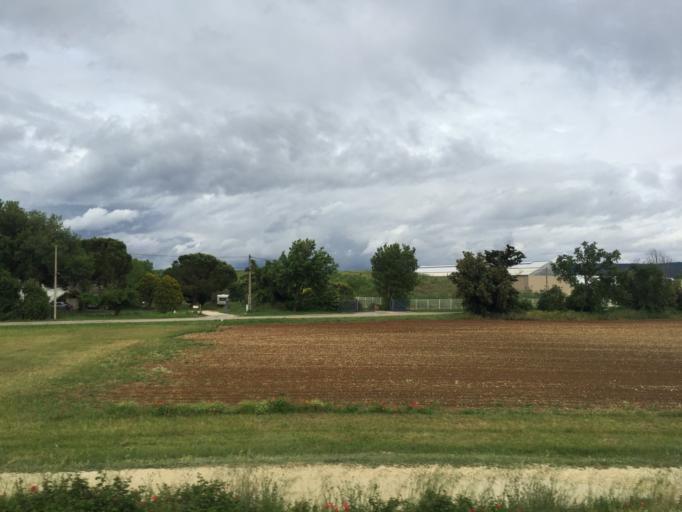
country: FR
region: Rhone-Alpes
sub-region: Departement de la Drome
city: Pierrelatte
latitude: 44.3577
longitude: 4.7015
